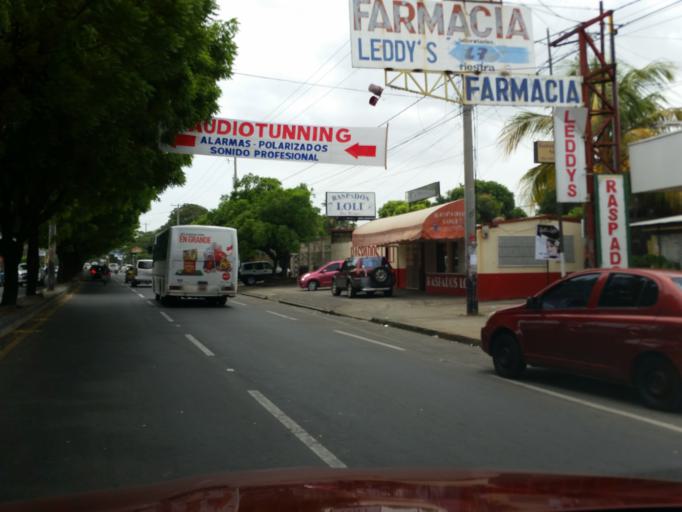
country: NI
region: Managua
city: Managua
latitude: 12.1260
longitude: -86.2931
